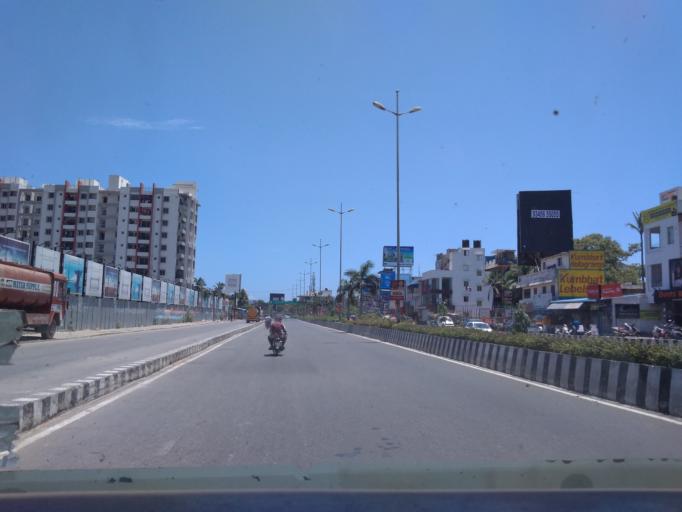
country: IN
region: Tamil Nadu
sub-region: Kancheepuram
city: Injambakkam
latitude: 12.8345
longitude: 80.2288
